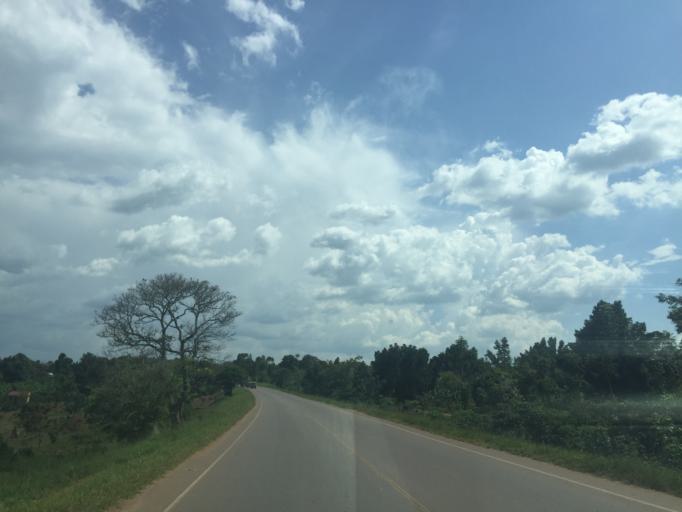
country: UG
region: Central Region
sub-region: Luwero District
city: Wobulenzi
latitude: 0.7607
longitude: 32.5133
